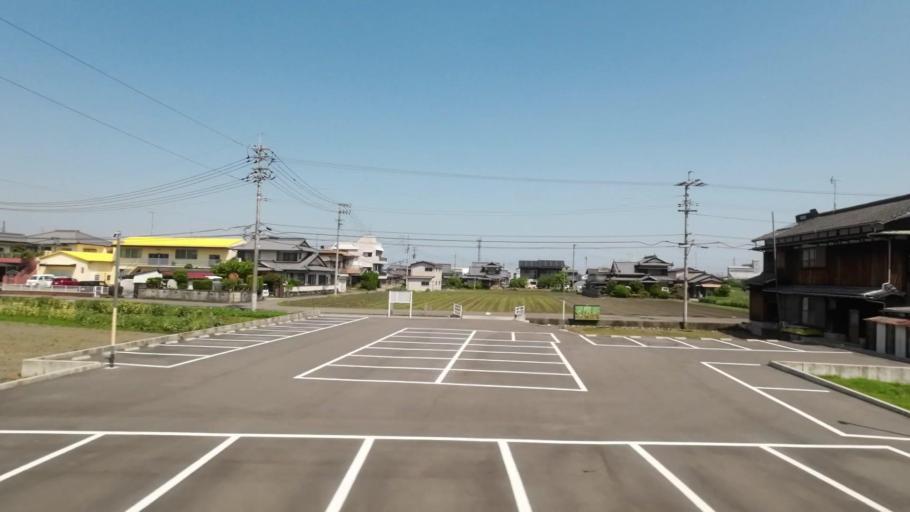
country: JP
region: Ehime
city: Saijo
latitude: 33.8993
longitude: 133.1711
